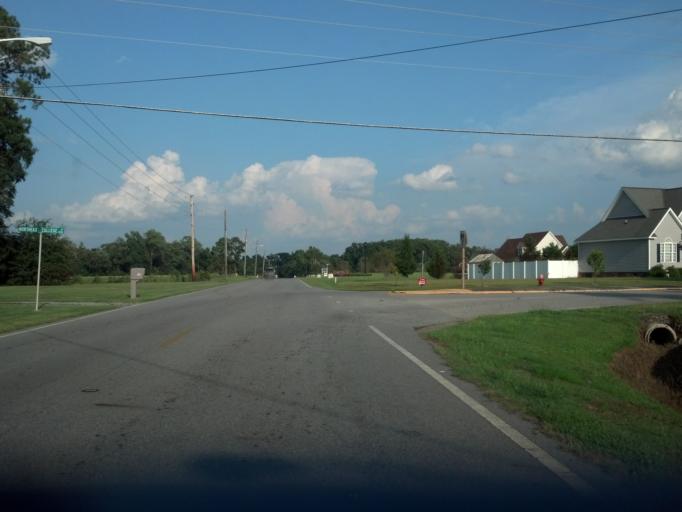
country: US
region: North Carolina
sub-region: Pitt County
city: Ayden
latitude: 35.4811
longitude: -77.4112
